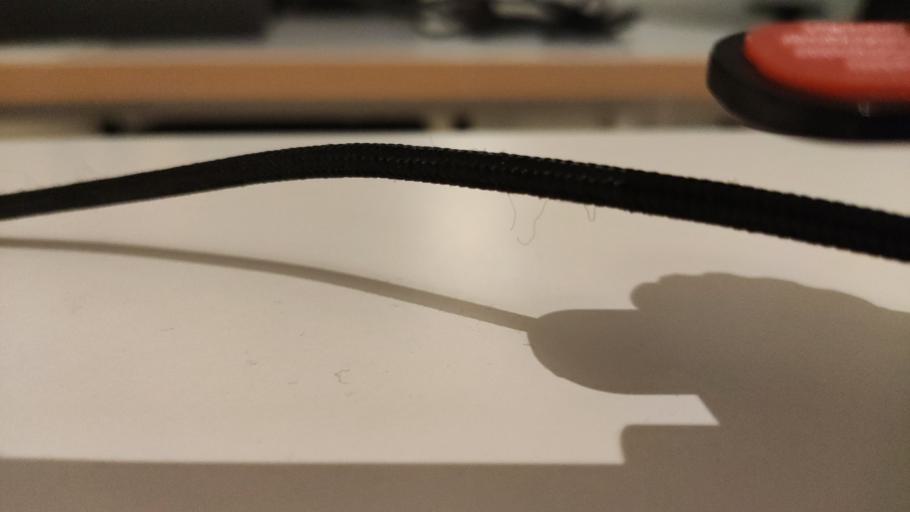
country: RU
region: Moskovskaya
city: Kurovskoye
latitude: 55.5859
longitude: 38.8940
